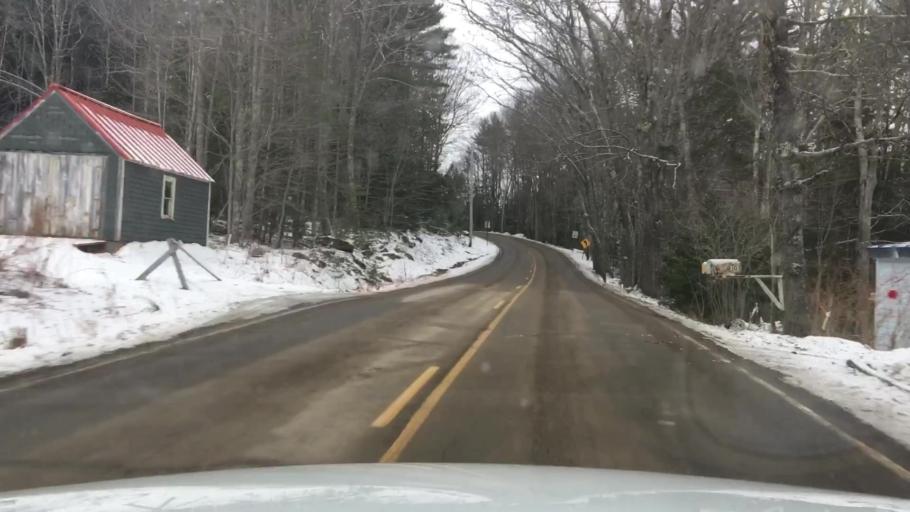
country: US
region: Maine
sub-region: Waldo County
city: Lincolnville
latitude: 44.2858
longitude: -69.0161
